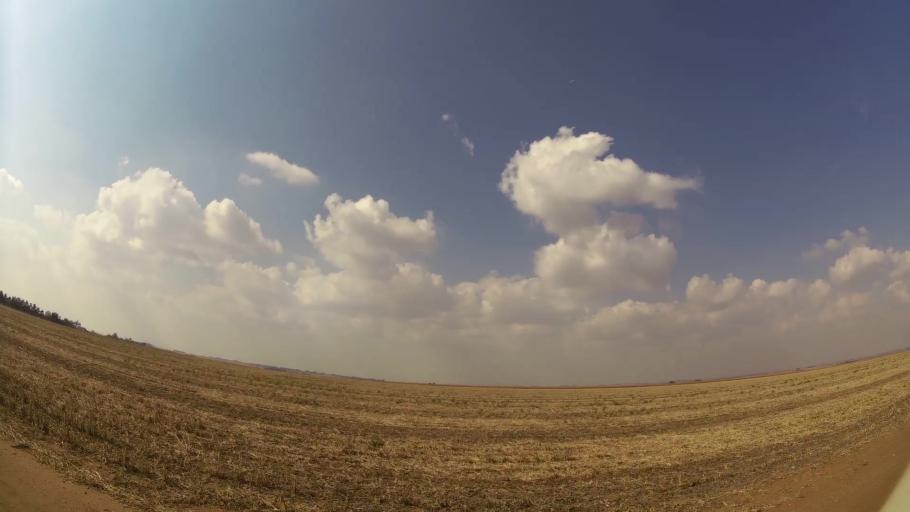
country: ZA
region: Mpumalanga
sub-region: Nkangala District Municipality
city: Delmas
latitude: -26.1933
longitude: 28.5478
